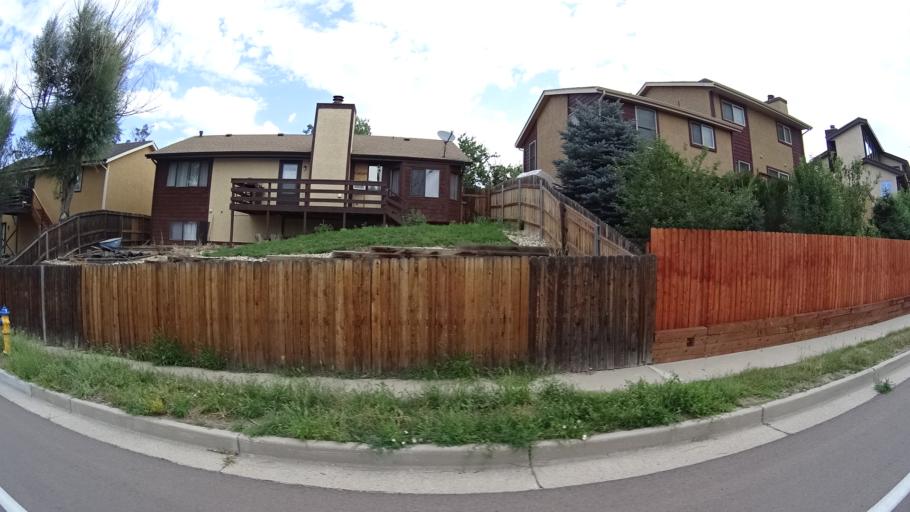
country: US
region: Colorado
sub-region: El Paso County
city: Cimarron Hills
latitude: 38.8959
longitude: -104.7324
